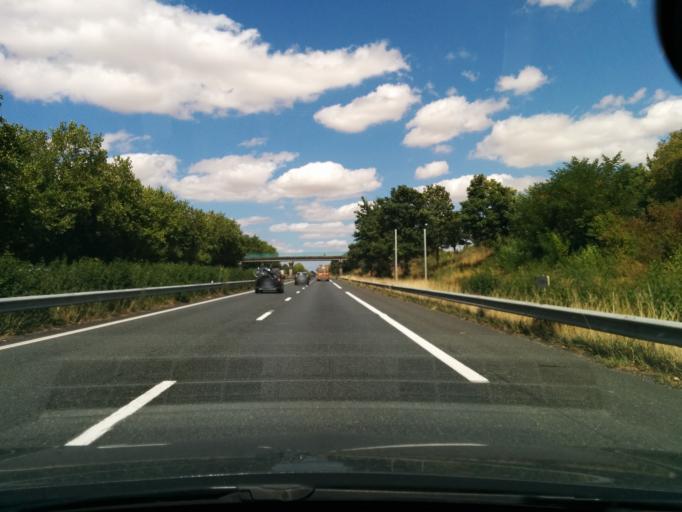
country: FR
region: Centre
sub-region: Departement de l'Indre
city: Montierchaume
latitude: 46.9022
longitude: 1.7340
